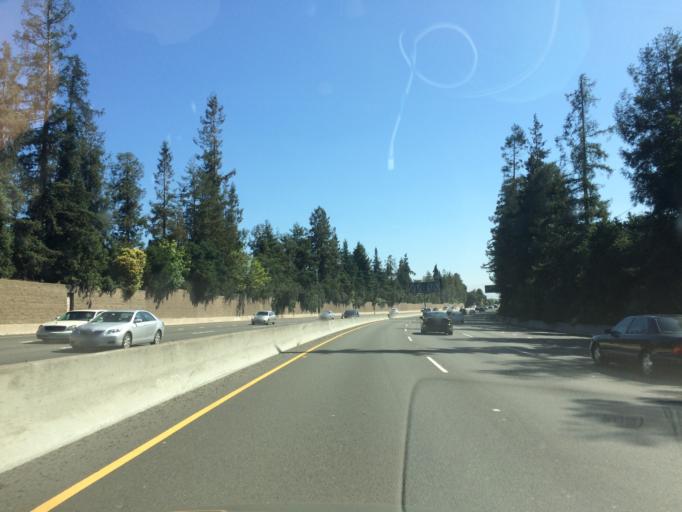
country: US
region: California
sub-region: Santa Clara County
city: Burbank
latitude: 37.3311
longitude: -121.9401
